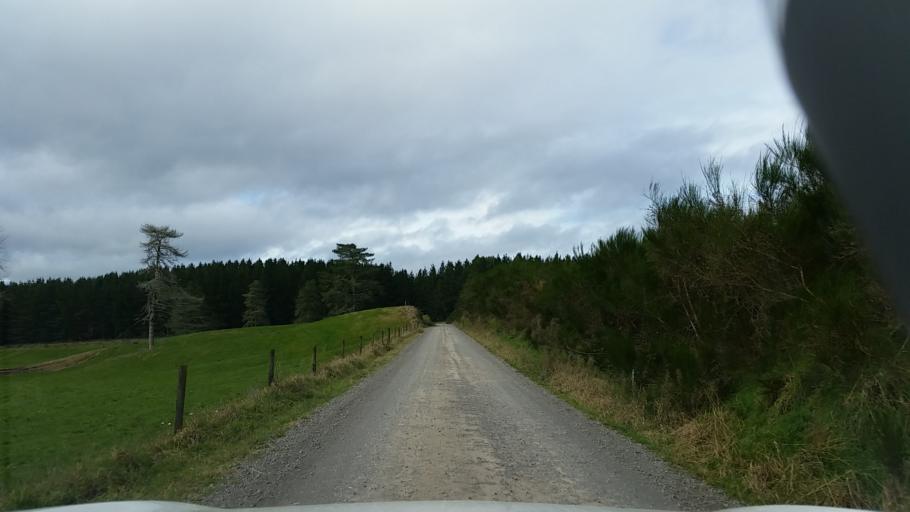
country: NZ
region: Bay of Plenty
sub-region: Whakatane District
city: Murupara
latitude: -38.3426
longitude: 176.5416
